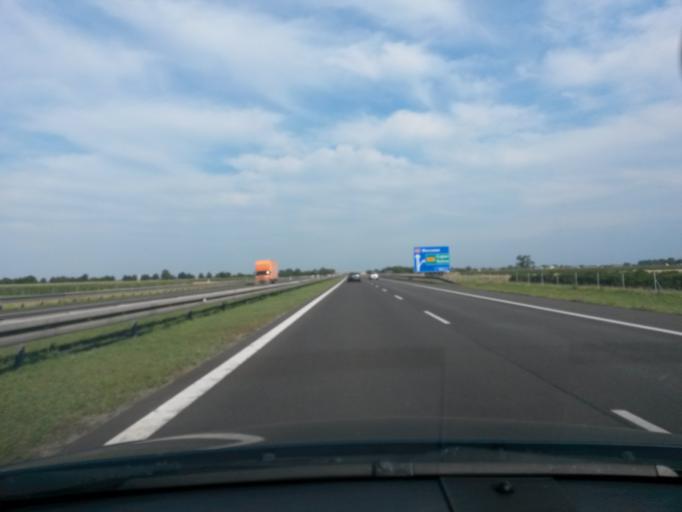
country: PL
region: Greater Poland Voivodeship
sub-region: Powiat slupecki
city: Ladek
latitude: 52.2107
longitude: 17.9947
